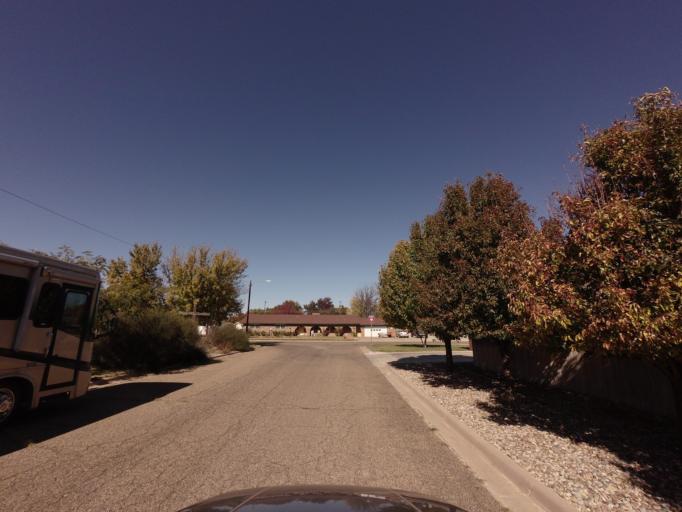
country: US
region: New Mexico
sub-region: Curry County
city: Clovis
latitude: 34.4203
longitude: -103.1909
